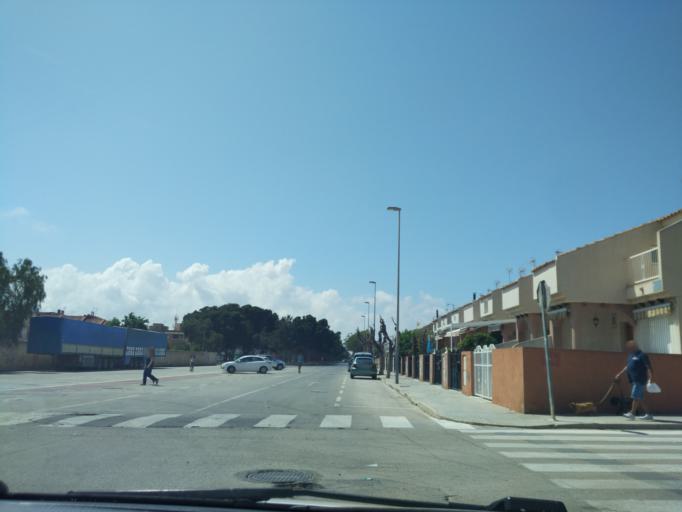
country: ES
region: Murcia
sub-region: Murcia
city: Los Alcazares
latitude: 37.7496
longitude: -0.8488
